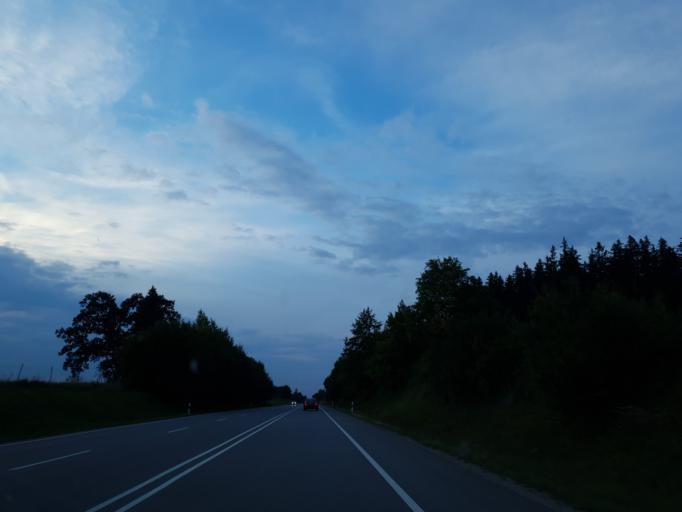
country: DE
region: Bavaria
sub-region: Swabia
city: Mauerstetten
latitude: 47.8460
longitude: 10.6712
